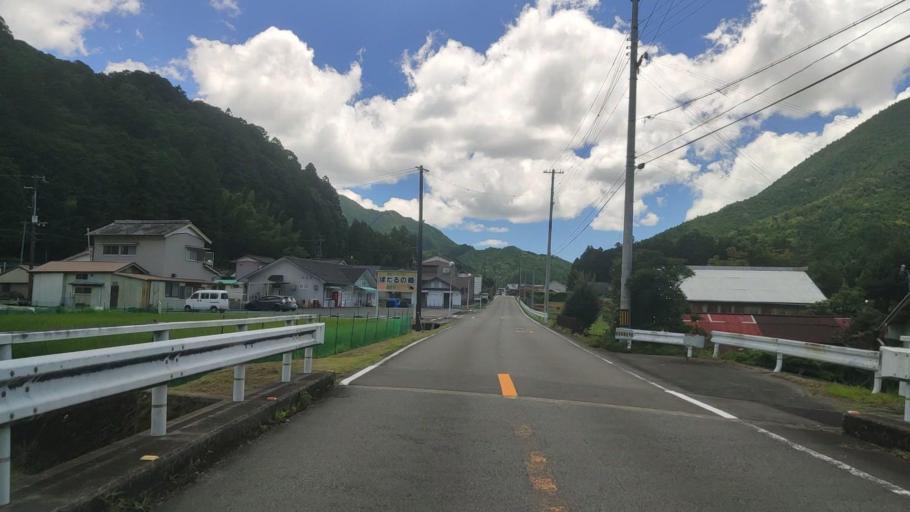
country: JP
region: Mie
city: Owase
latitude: 33.9797
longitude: 136.0508
